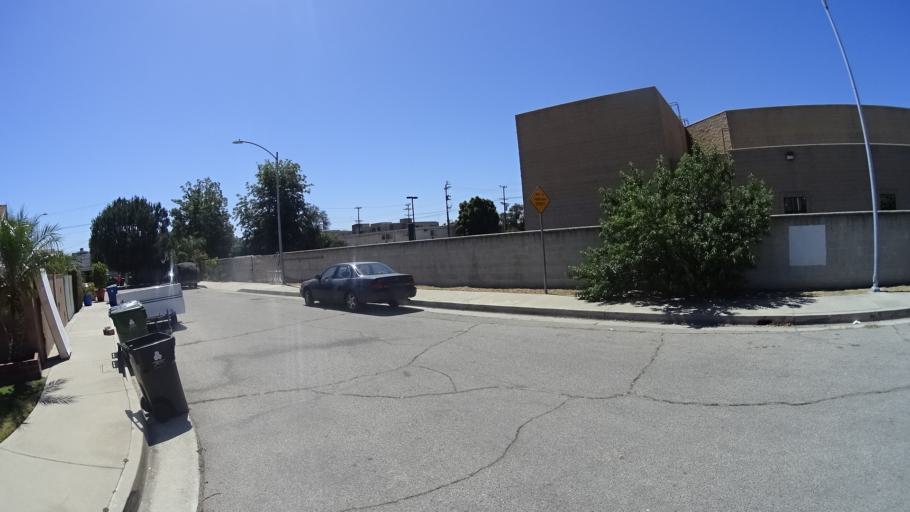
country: US
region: California
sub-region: Los Angeles County
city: Van Nuys
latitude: 34.1948
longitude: -118.4959
